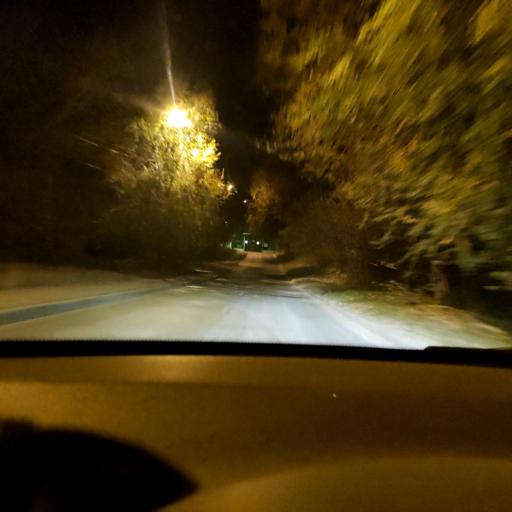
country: RU
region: Samara
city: Samara
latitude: 53.2461
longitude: 50.1740
